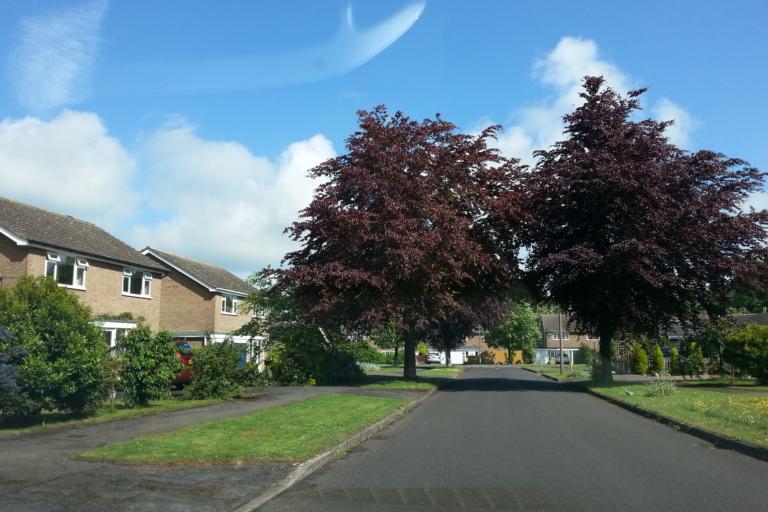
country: GB
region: England
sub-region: District of Rutland
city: Clipsham
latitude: 52.8074
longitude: -0.6153
